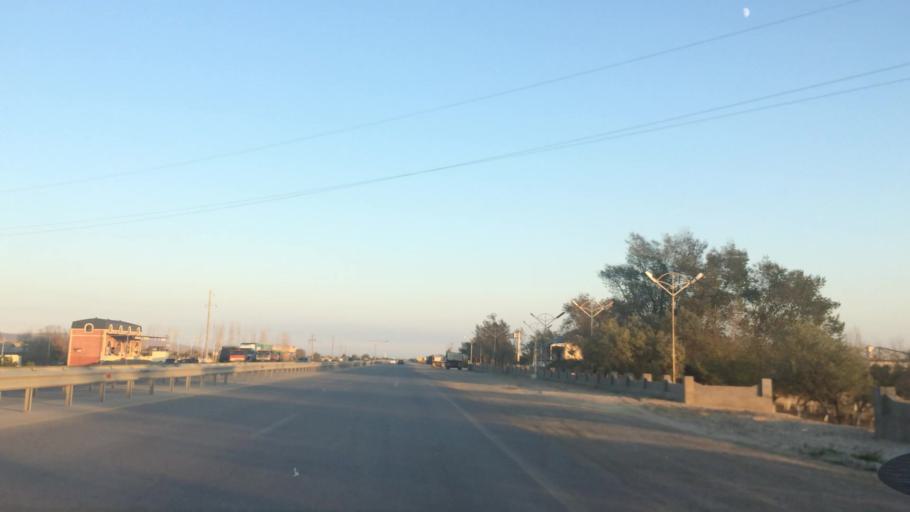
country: AZ
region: Haciqabul
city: Haciqabul
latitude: 40.0104
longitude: 49.1497
